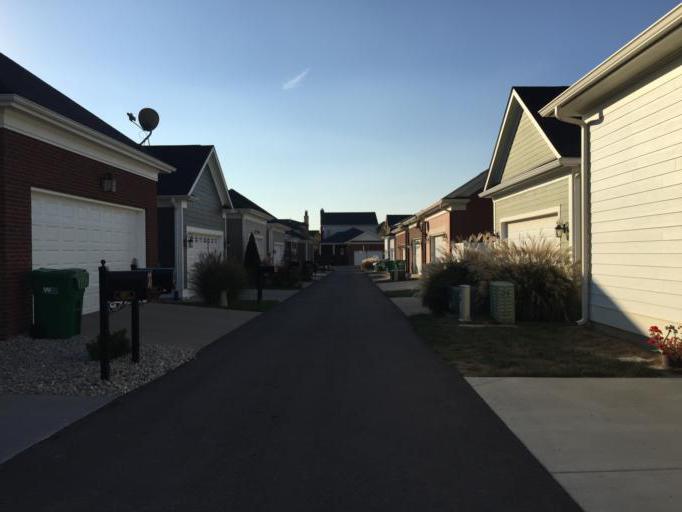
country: US
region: Kentucky
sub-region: Jefferson County
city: Worthington
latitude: 38.3269
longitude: -85.5651
